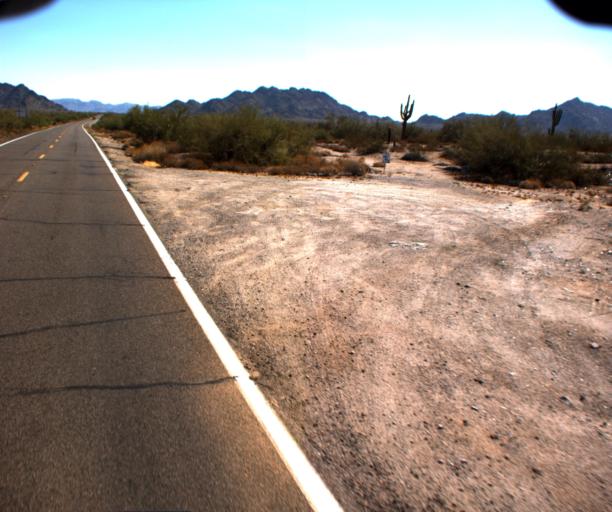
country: US
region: Arizona
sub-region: Pinal County
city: Sacaton
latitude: 33.0119
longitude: -111.7476
